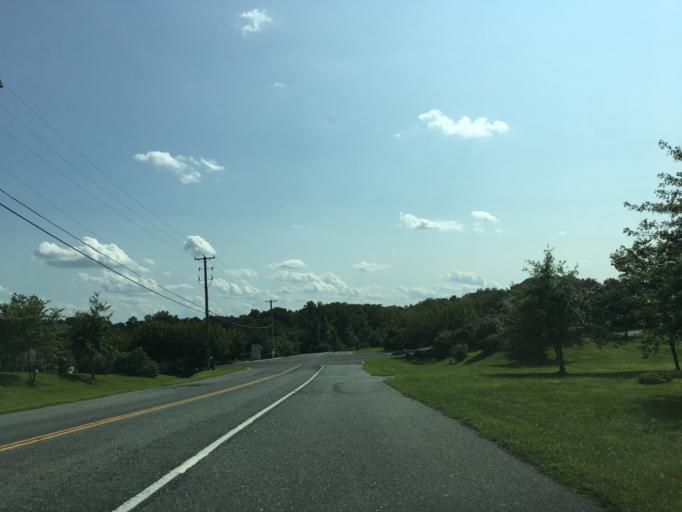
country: US
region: Maryland
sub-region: Cecil County
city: North East
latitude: 39.5284
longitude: -75.9011
